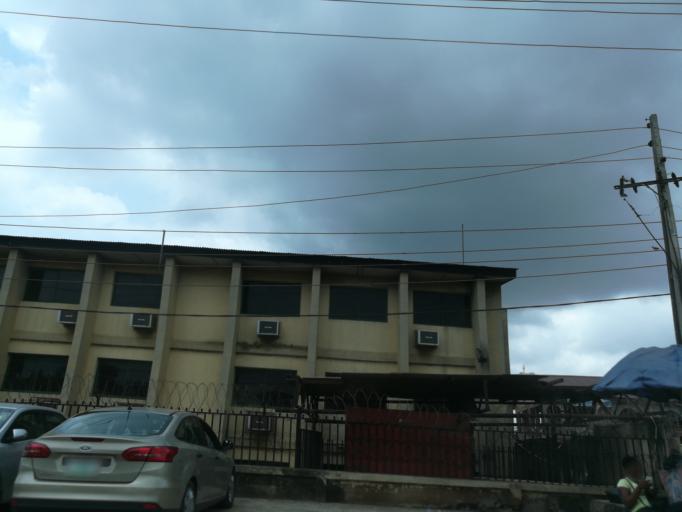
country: NG
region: Lagos
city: Agege
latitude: 6.6092
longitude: 3.3301
